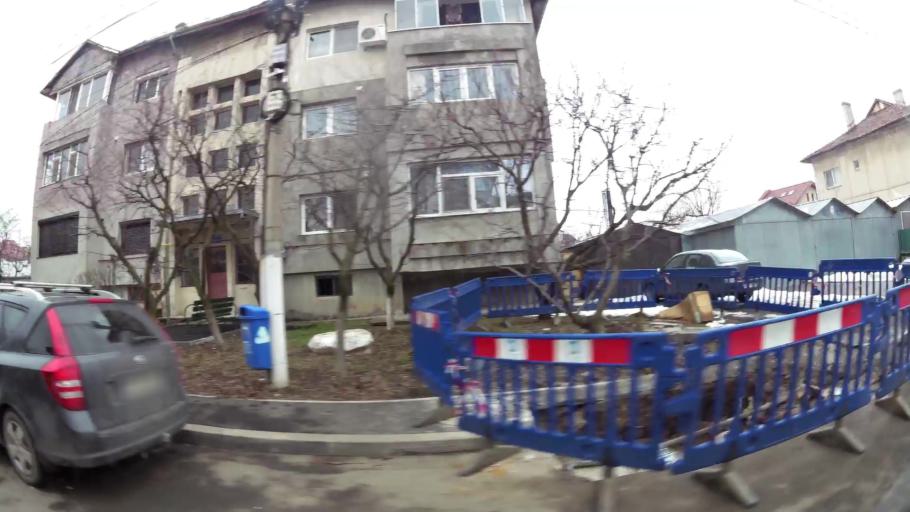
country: RO
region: Ilfov
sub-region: Comuna Otopeni
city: Otopeni
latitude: 44.5522
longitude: 26.0758
